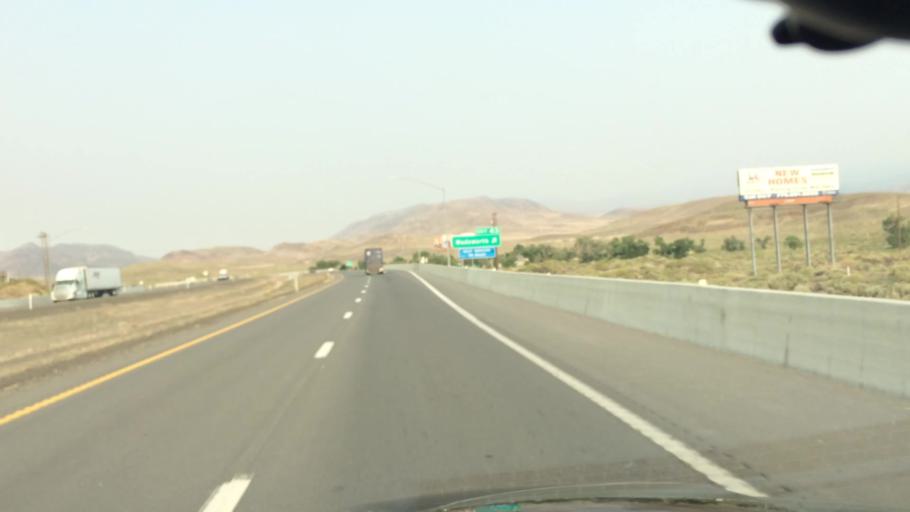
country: US
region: Nevada
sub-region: Lyon County
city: Fernley
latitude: 39.6172
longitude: -119.3035
